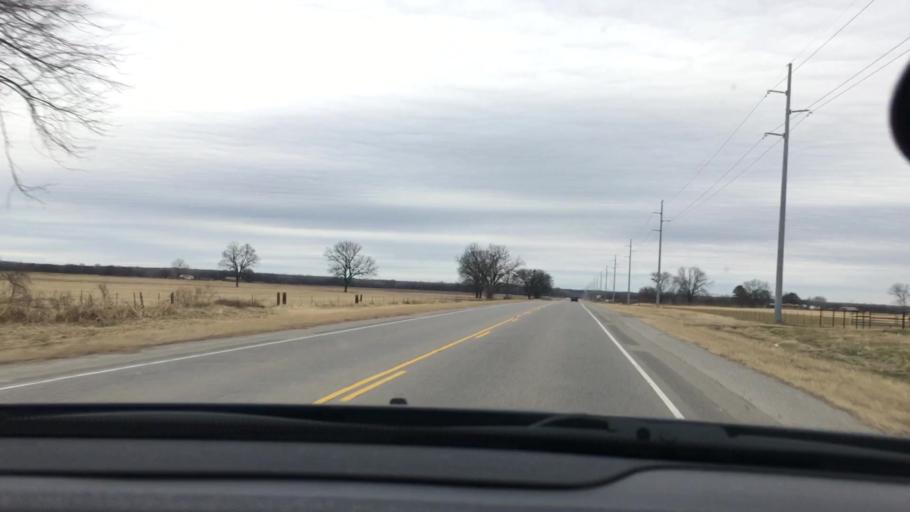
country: US
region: Oklahoma
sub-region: Marshall County
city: Oakland
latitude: 34.1952
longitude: -96.8022
